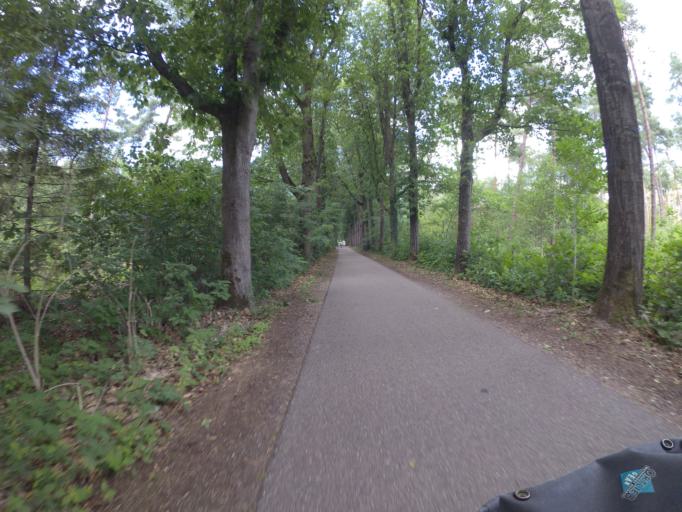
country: NL
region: North Brabant
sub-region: Gemeente Oisterwijk
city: Oisterwijk
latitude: 51.5643
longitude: 5.1839
